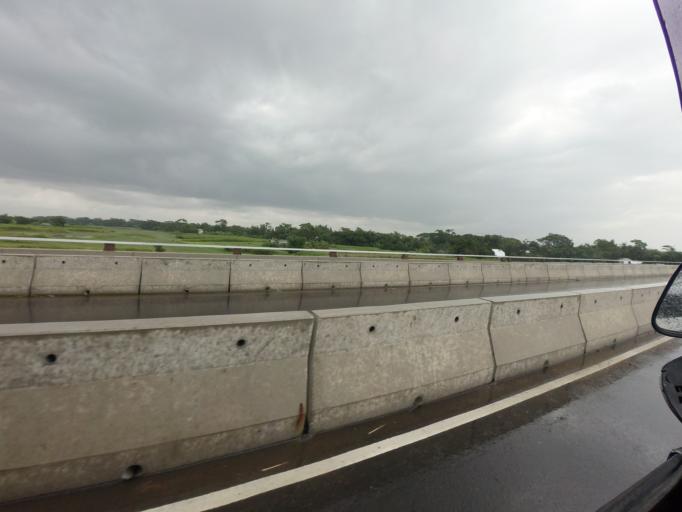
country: BD
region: Dhaka
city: Char Bhadrasan
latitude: 23.3996
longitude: 90.2138
